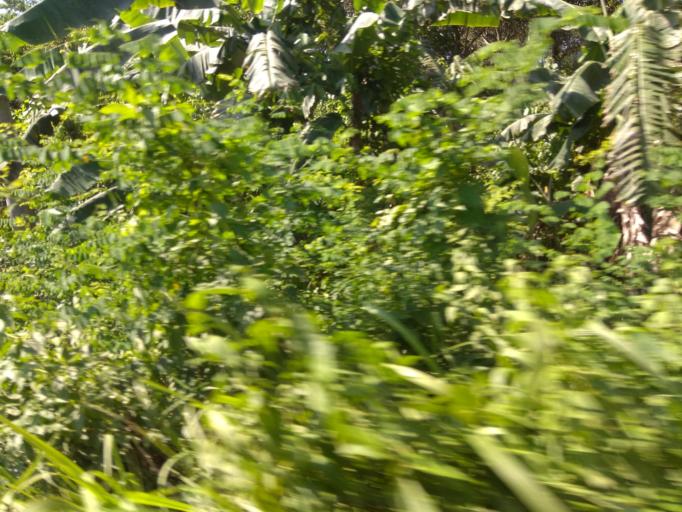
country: BD
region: Chittagong
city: Khagrachhari
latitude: 23.0300
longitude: 92.0131
